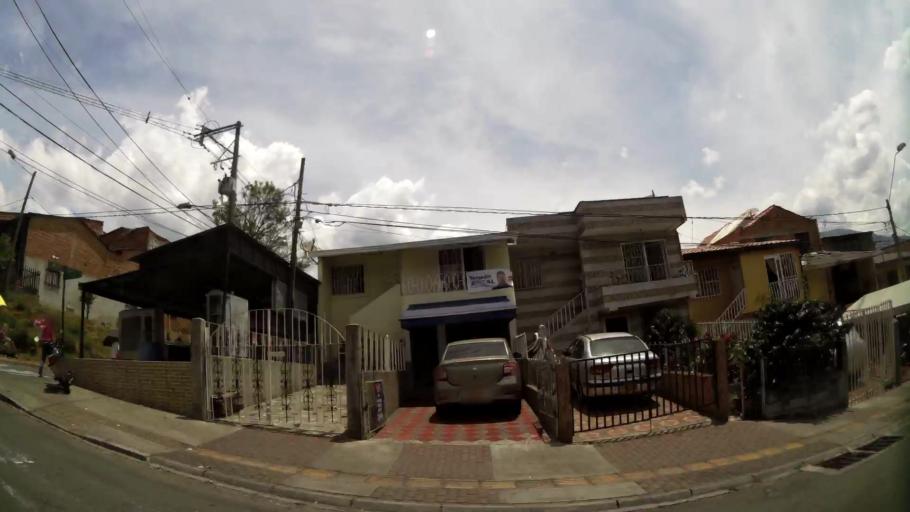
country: CO
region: Antioquia
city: Bello
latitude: 6.3445
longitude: -75.5554
